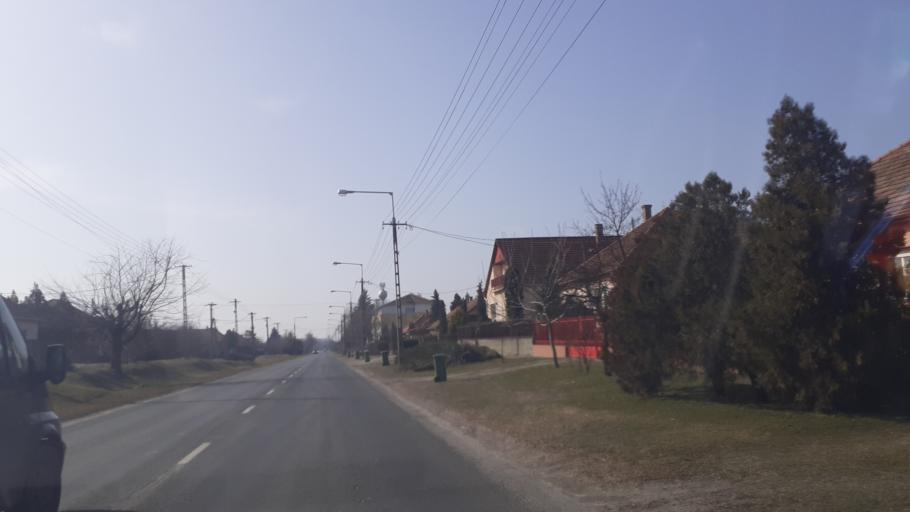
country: HU
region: Pest
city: Orkeny
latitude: 47.1346
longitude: 19.4388
